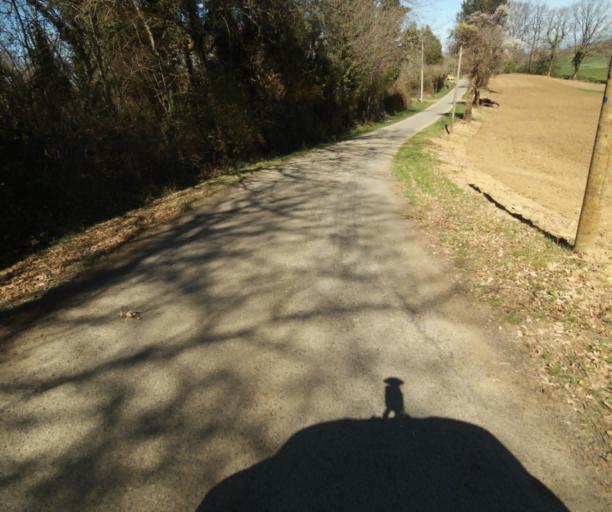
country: FR
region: Limousin
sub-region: Departement de la Correze
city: Uzerche
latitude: 45.3918
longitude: 1.6071
